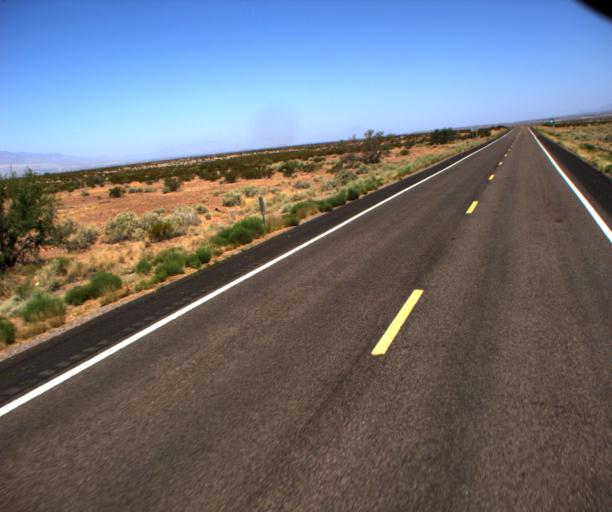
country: US
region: Arizona
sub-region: Graham County
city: Safford
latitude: 32.7861
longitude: -109.5425
